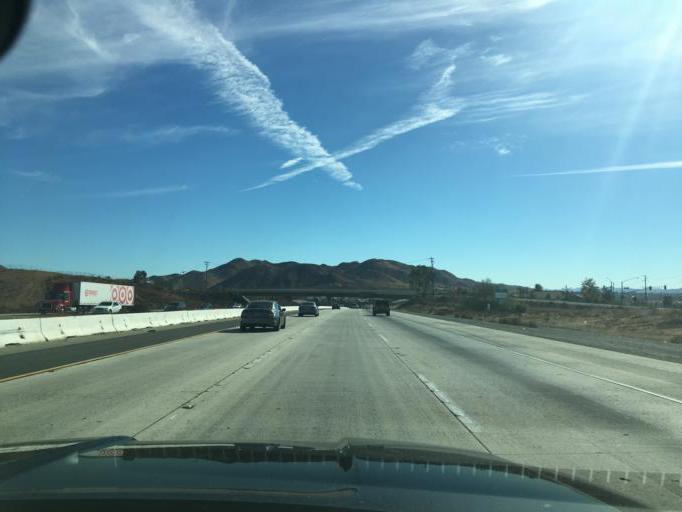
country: US
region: California
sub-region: Riverside County
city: Lake Elsinore
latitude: 33.6705
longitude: -117.3104
